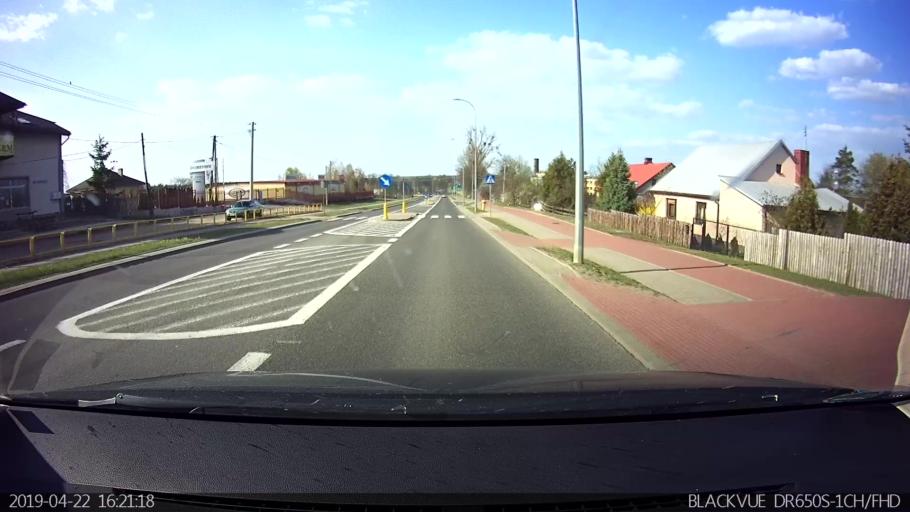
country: PL
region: Podlasie
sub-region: Powiat hajnowski
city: Kleszczele
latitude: 52.5612
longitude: 23.3181
